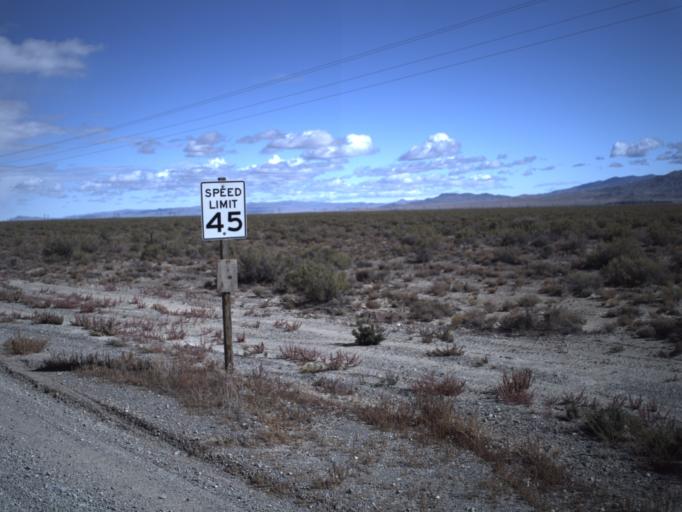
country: US
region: Nevada
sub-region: White Pine County
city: McGill
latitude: 39.0581
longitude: -114.0366
